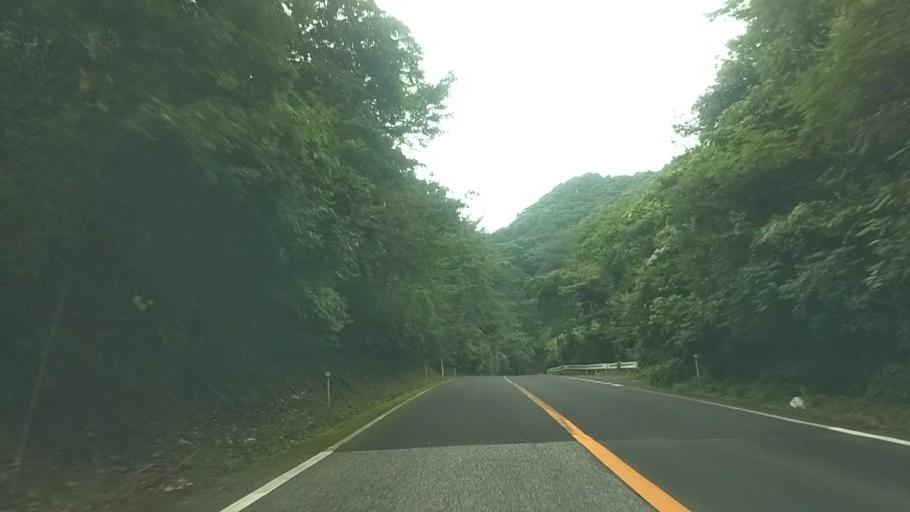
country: JP
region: Chiba
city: Kawaguchi
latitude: 35.2229
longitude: 140.0363
